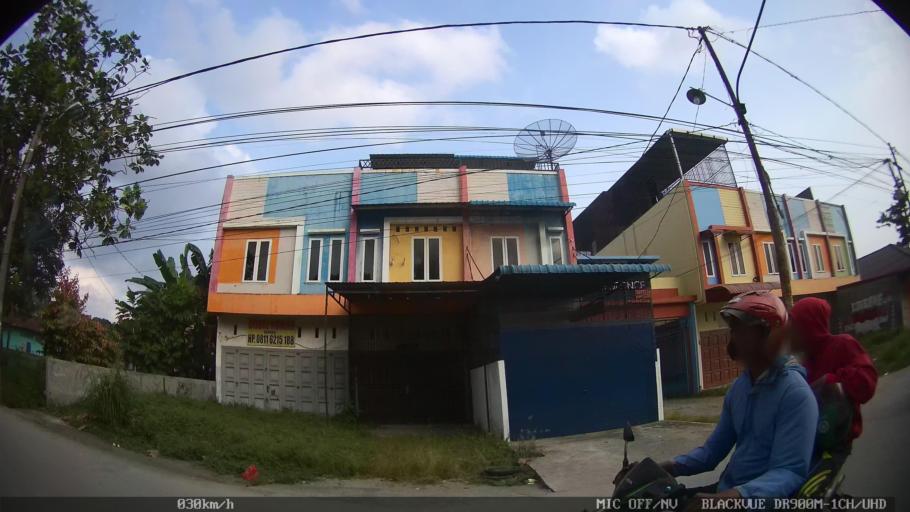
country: ID
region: North Sumatra
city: Medan
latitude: 3.5834
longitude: 98.7315
